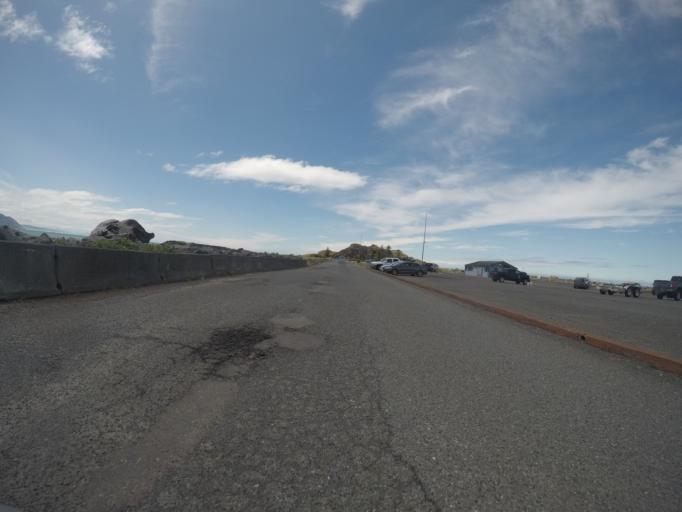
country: US
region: California
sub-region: Del Norte County
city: Crescent City
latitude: 41.7425
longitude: -124.1816
